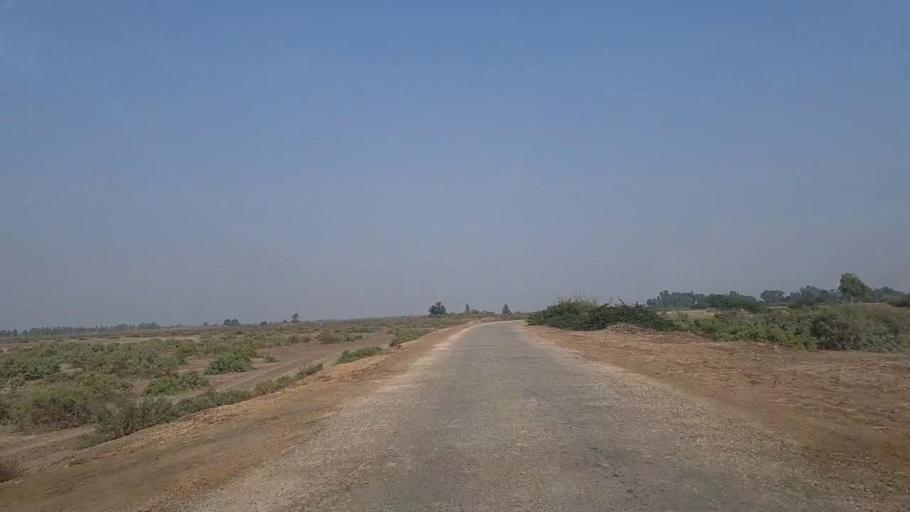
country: PK
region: Sindh
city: Keti Bandar
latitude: 24.2459
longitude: 67.6949
